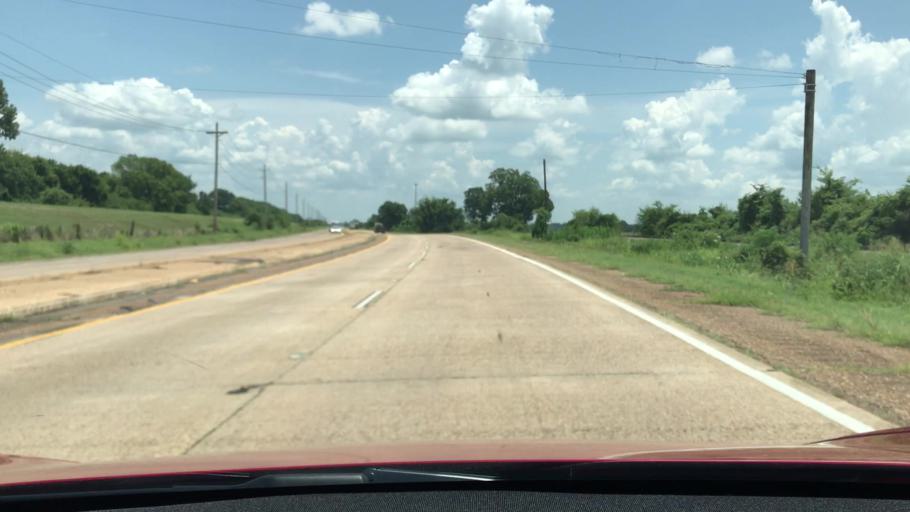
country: US
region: Louisiana
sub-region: Bossier Parish
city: Bossier City
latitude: 32.3887
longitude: -93.6817
